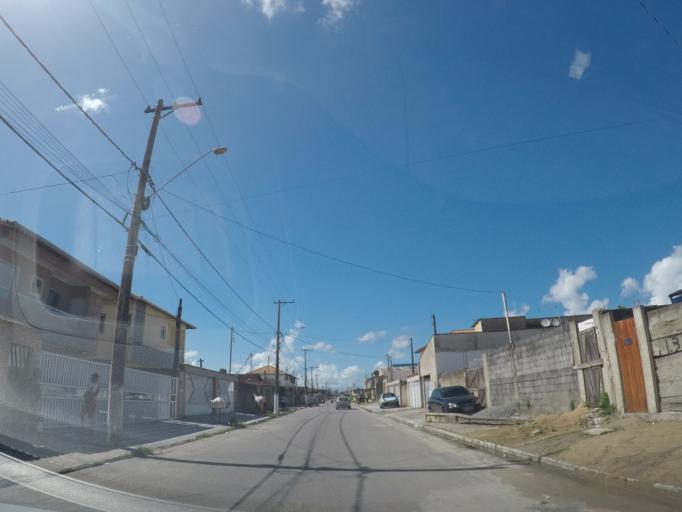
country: BR
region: Sao Paulo
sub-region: Praia Grande
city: Praia Grande
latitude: -24.0236
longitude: -46.5182
